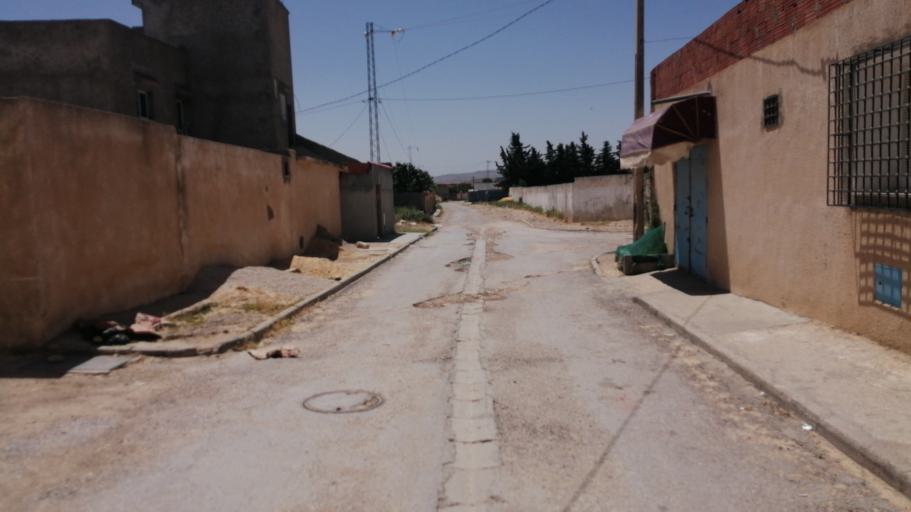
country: TN
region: Silyanah
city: Maktar
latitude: 35.8494
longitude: 9.2042
